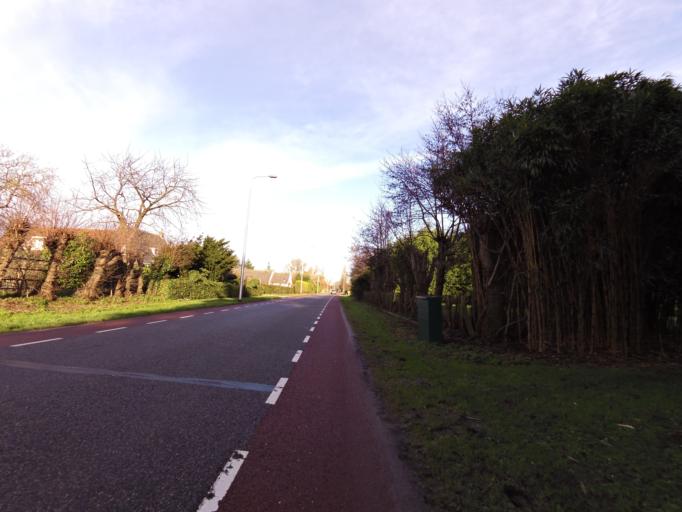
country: NL
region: South Holland
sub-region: Gemeente Hellevoetsluis
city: Nieuw-Helvoet
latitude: 51.8877
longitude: 4.0837
